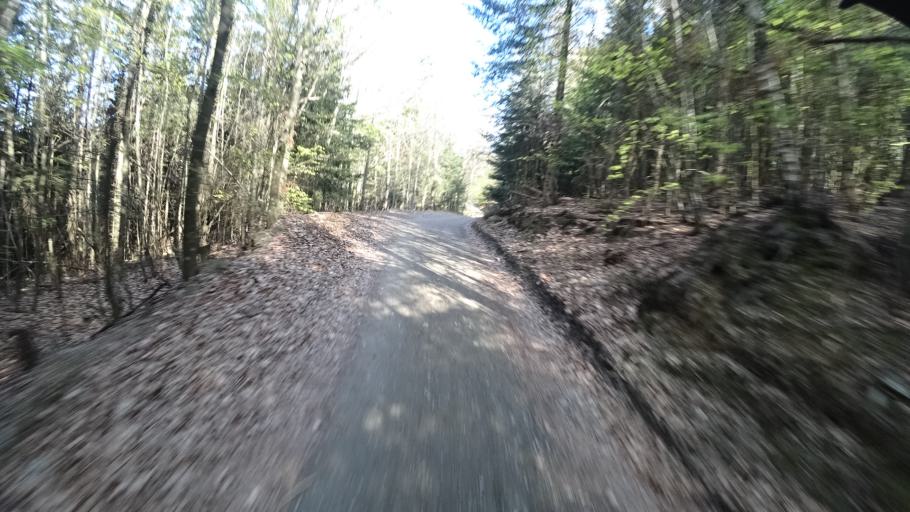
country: HR
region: Zagrebacka
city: Jablanovec
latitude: 45.8909
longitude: 15.9235
